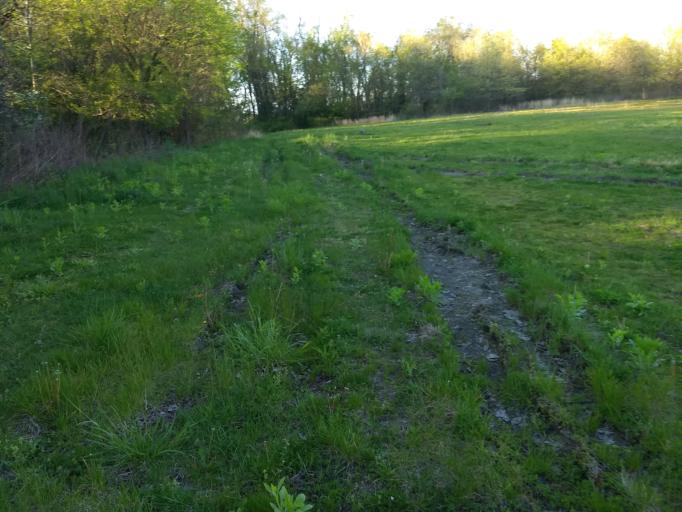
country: US
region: Pennsylvania
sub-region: Allegheny County
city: Green Tree
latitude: 40.4197
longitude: -80.0212
